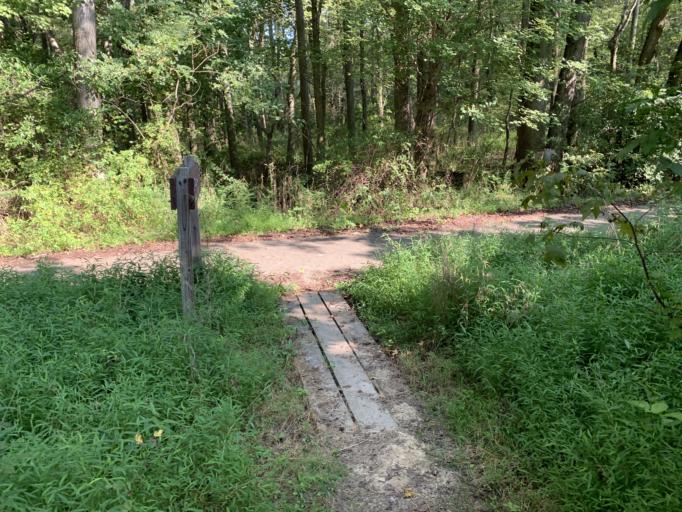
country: US
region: Maryland
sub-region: Baltimore County
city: Bowleys Quarters
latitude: 39.3528
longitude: -76.3679
